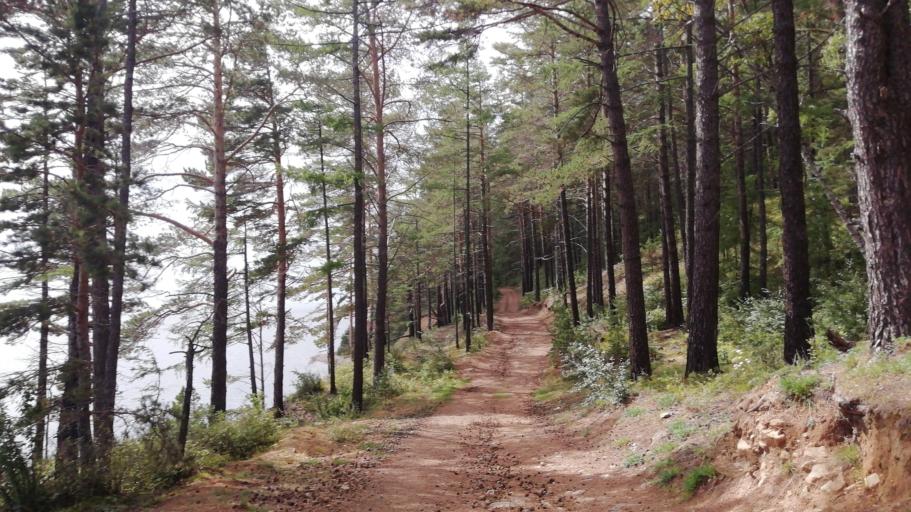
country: RU
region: Irkutsk
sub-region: Irkutskiy Rayon
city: Listvyanka
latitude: 51.8925
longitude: 105.0463
